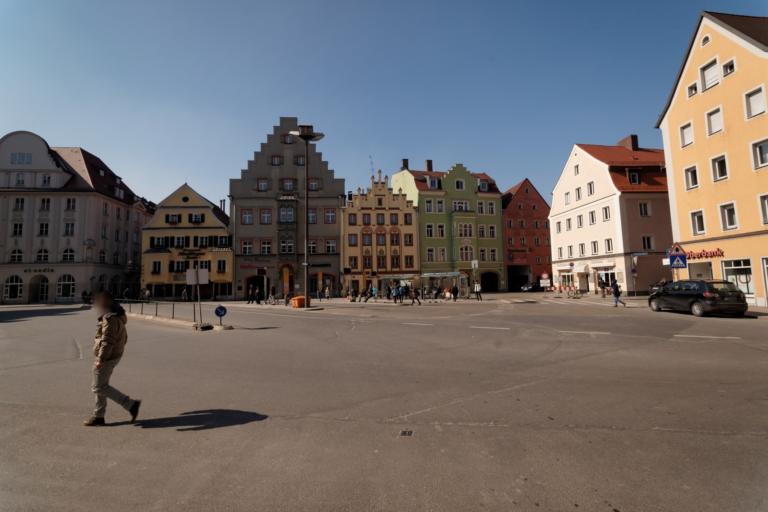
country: DE
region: Bavaria
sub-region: Upper Palatinate
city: Lappersdorf
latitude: 49.0199
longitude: 12.0900
